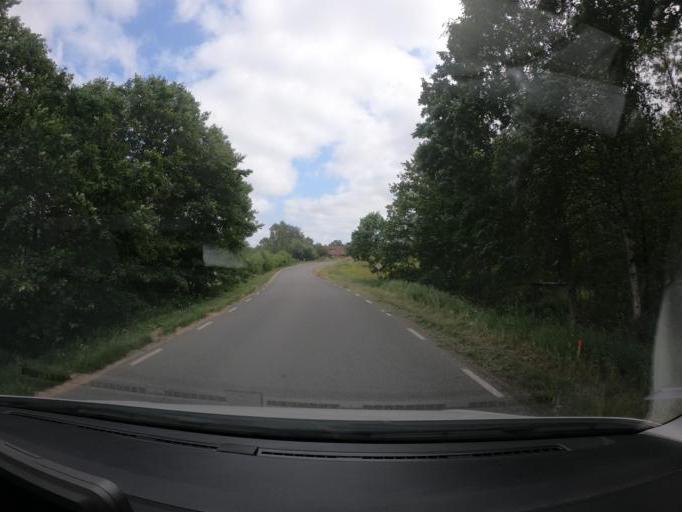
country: SE
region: Skane
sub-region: Hassleholms Kommun
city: Tormestorp
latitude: 56.1425
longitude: 13.6280
